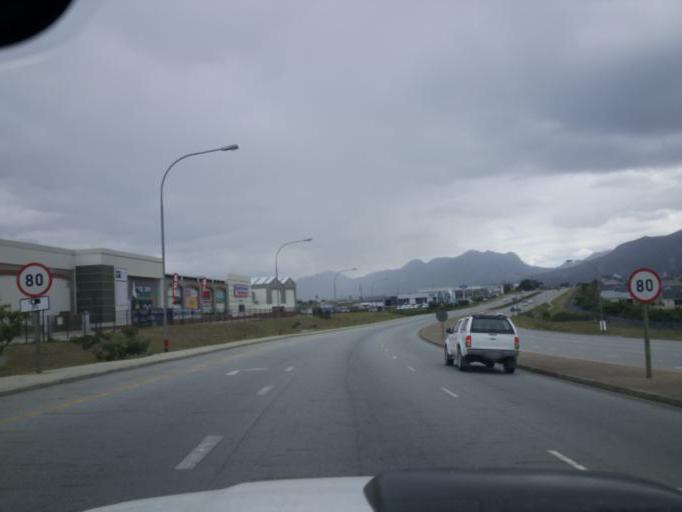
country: ZA
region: Western Cape
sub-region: Eden District Municipality
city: George
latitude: -33.9837
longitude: 22.5013
